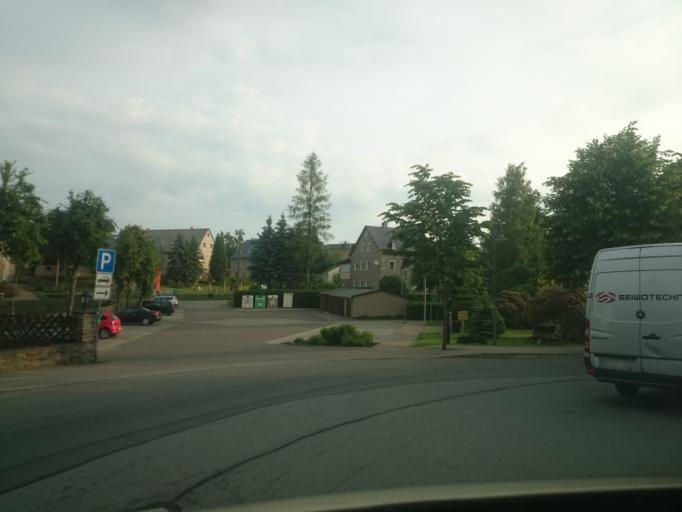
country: DE
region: Saxony
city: Grossolbersdorf
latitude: 50.6928
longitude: 13.0880
